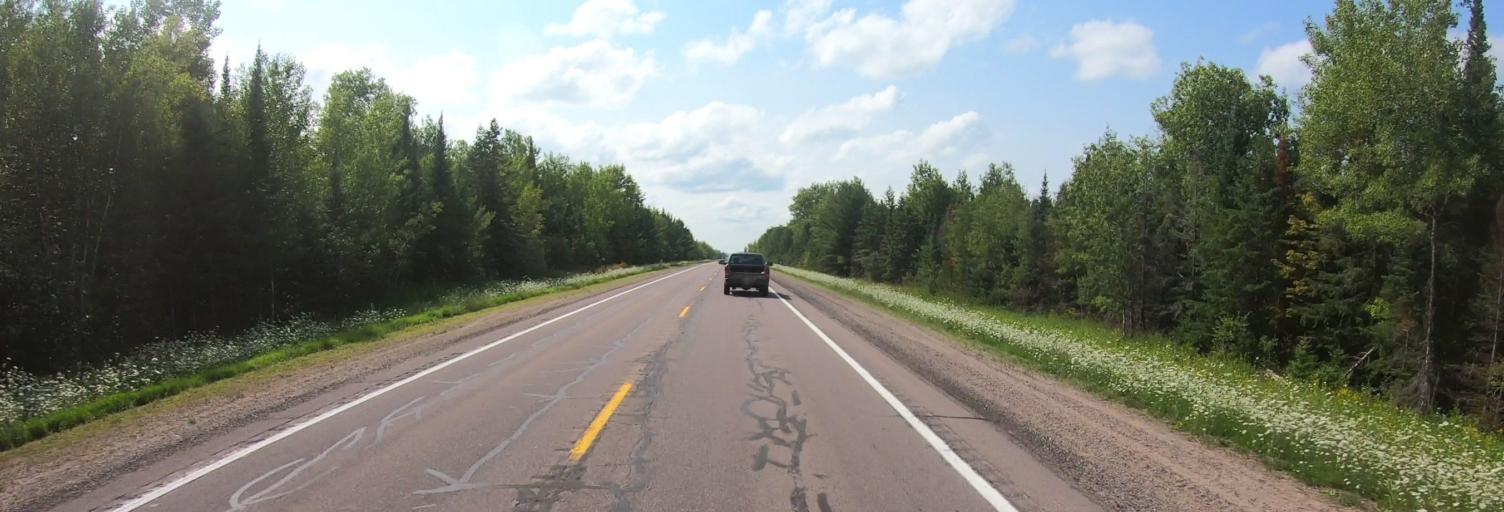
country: US
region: Michigan
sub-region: Ontonagon County
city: Ontonagon
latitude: 46.5465
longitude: -89.3526
